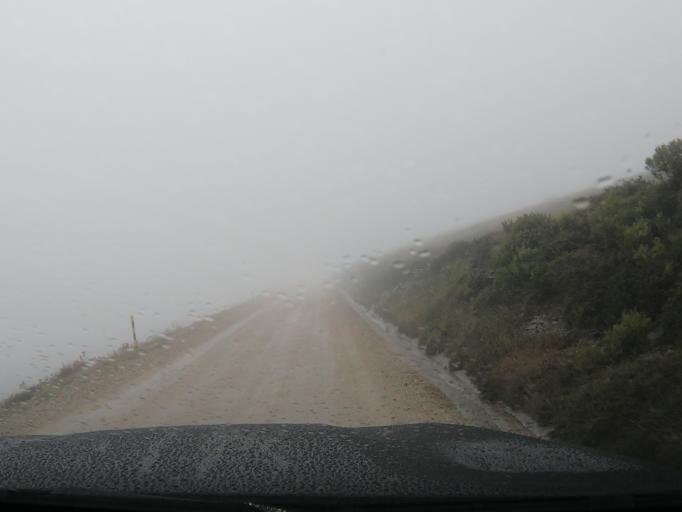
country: PT
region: Vila Real
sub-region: Vila Real
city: Vila Real
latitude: 41.3295
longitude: -7.8345
